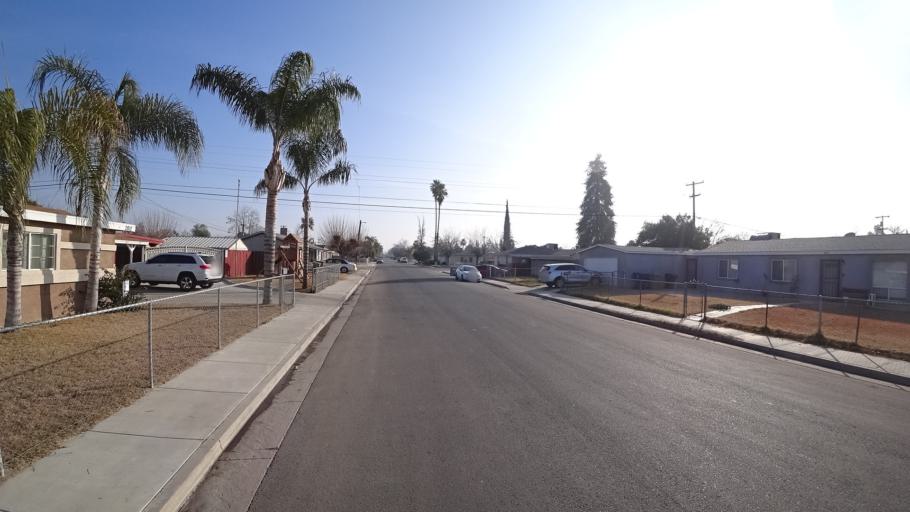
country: US
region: California
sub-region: Kern County
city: Bakersfield
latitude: 35.3341
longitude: -119.0344
